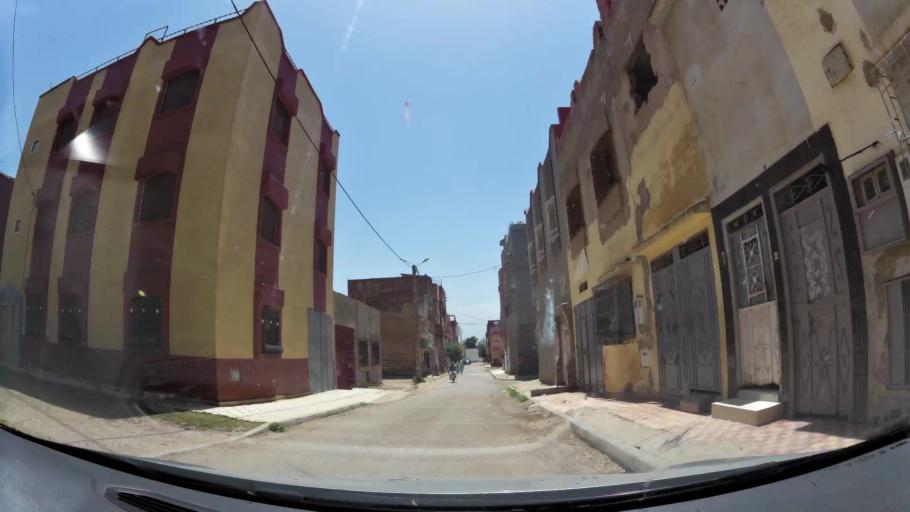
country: MA
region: Rabat-Sale-Zemmour-Zaer
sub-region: Khemisset
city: Khemisset
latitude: 33.8334
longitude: -6.0695
